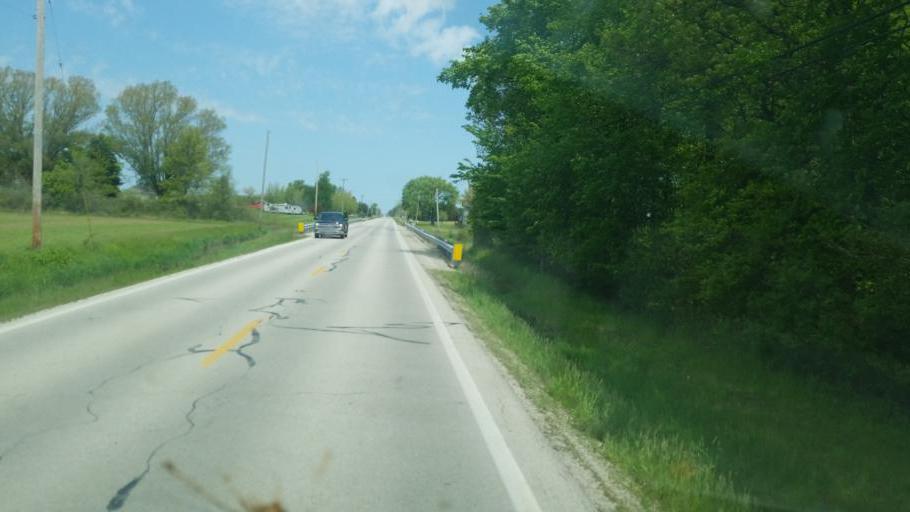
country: US
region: Ohio
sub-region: Ottawa County
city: Oak Harbor
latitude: 41.5534
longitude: -83.1448
